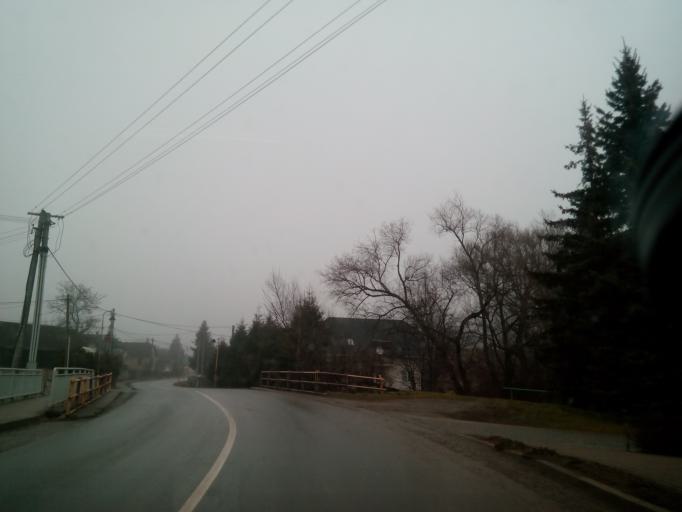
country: SK
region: Kosicky
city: Krompachy
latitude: 48.9968
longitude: 20.9426
